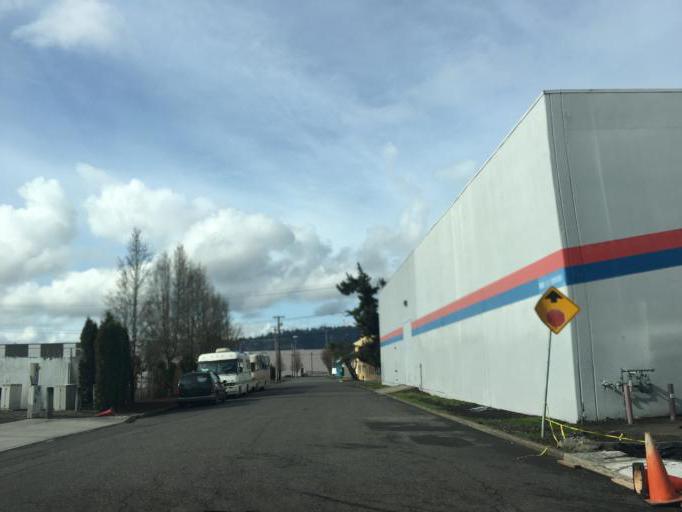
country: US
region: Oregon
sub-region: Clackamas County
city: Milwaukie
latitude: 45.4871
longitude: -122.6385
